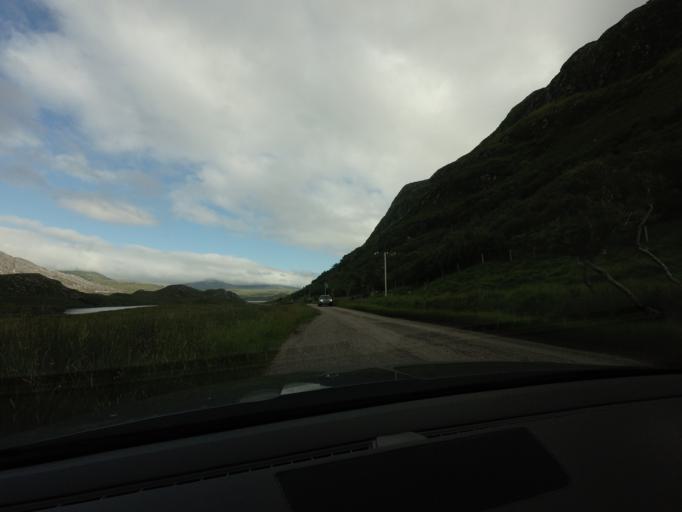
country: GB
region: Scotland
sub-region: Highland
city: Ullapool
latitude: 58.3438
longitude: -4.9541
